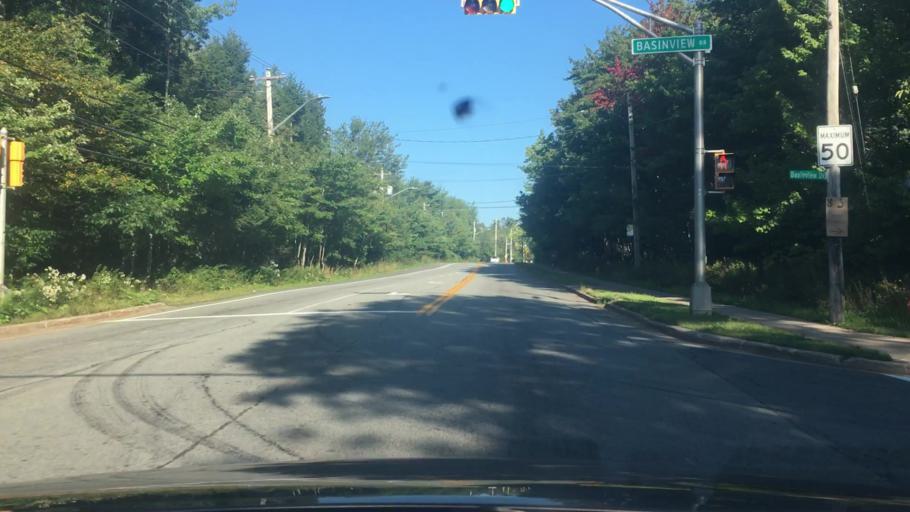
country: CA
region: Nova Scotia
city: Dartmouth
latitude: 44.7171
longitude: -63.6831
